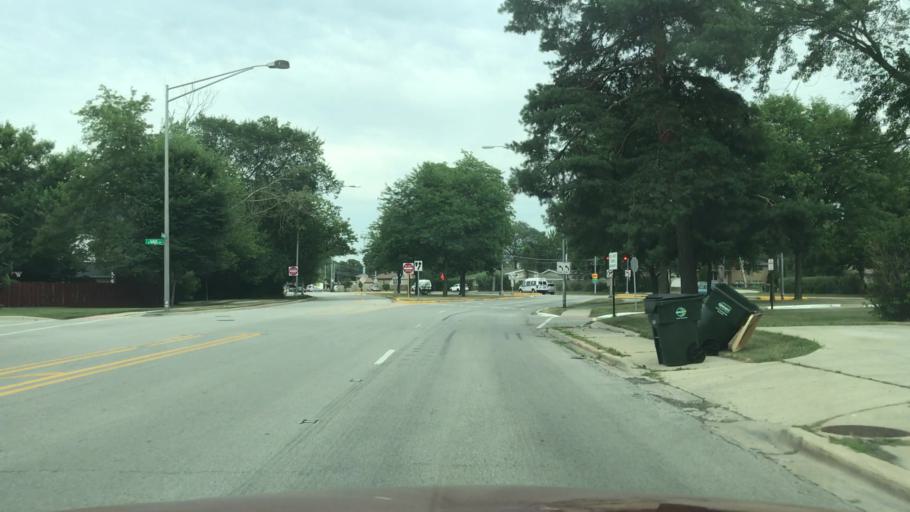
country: US
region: Illinois
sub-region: Cook County
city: Arlington Heights
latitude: 42.0672
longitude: -87.9846
